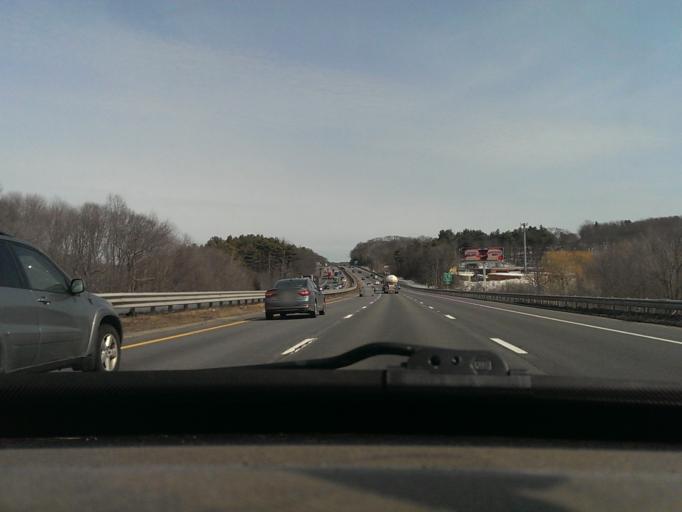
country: US
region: Massachusetts
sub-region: Worcester County
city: Auburn
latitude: 42.2028
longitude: -71.8212
